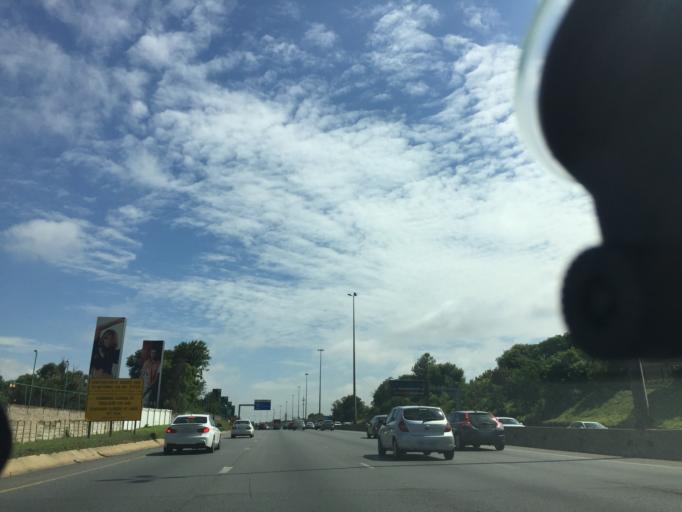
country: ZA
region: Gauteng
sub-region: City of Johannesburg Metropolitan Municipality
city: Johannesburg
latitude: -26.1182
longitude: 28.0738
